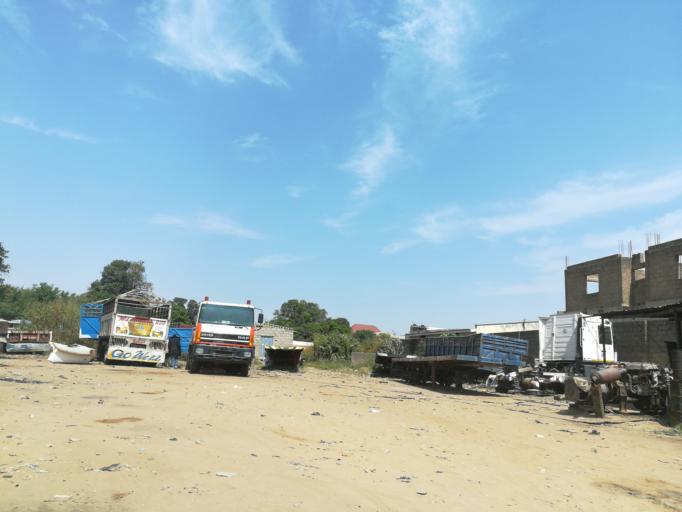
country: NG
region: Kano
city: Kano
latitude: 12.0292
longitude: 8.5200
